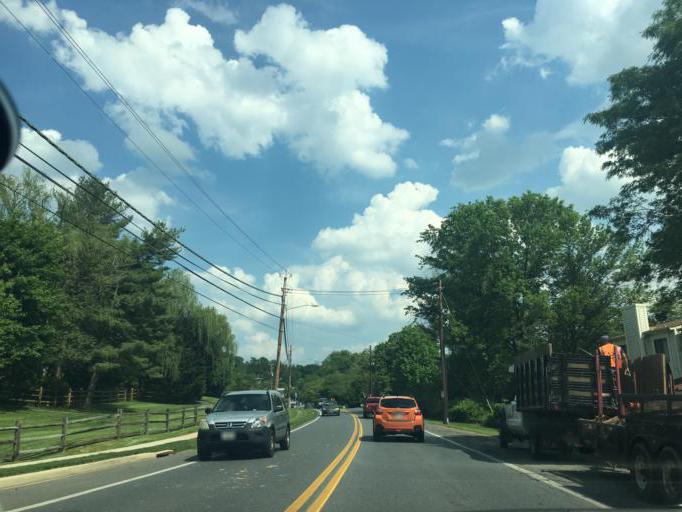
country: US
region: Maryland
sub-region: Montgomery County
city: Montgomery Village
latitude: 39.1891
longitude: -77.1904
